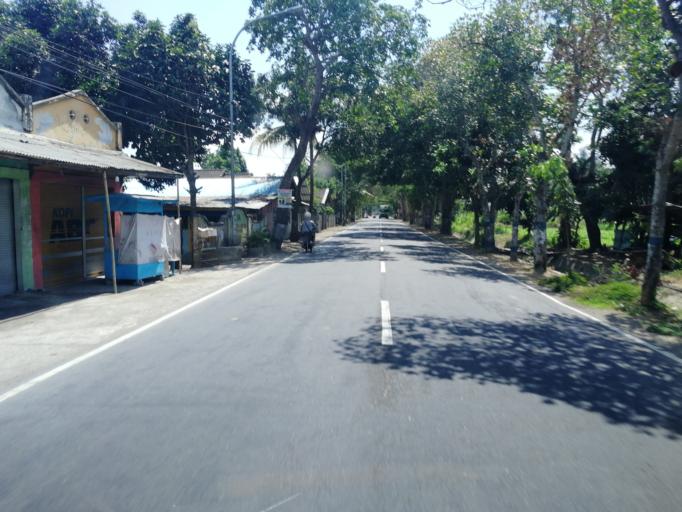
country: ID
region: West Nusa Tenggara
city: Jelateng Timur
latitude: -8.7022
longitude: 116.0962
